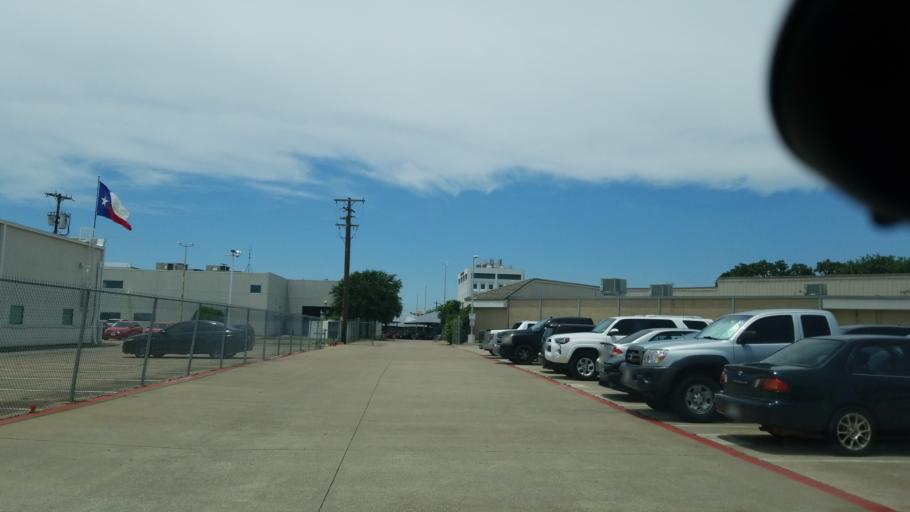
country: US
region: Texas
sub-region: Dallas County
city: Irving
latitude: 32.8384
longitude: -96.9713
